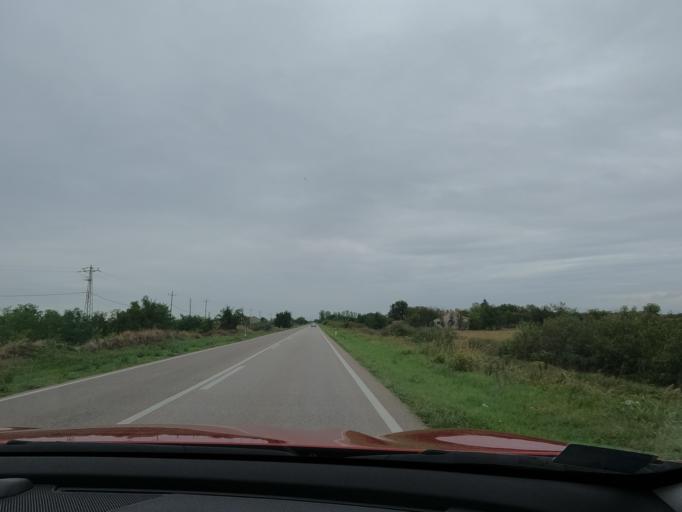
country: RS
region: Autonomna Pokrajina Vojvodina
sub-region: Severnobanatski Okrug
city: Kikinda
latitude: 45.7686
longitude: 20.4237
